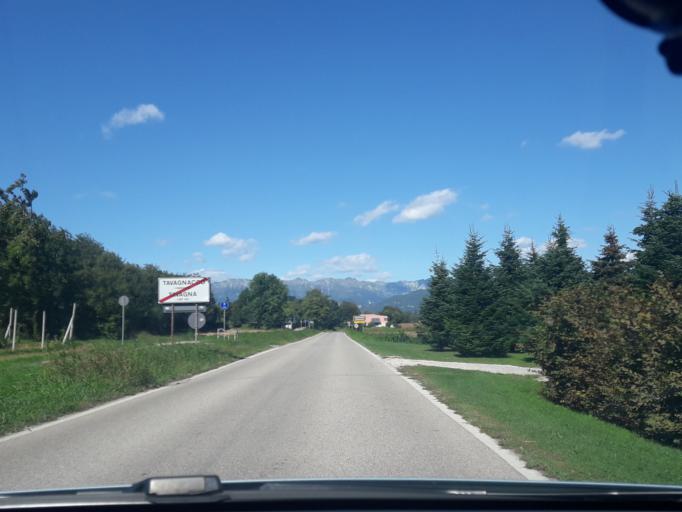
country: IT
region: Friuli Venezia Giulia
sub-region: Provincia di Udine
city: Reana del Roiale
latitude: 46.1349
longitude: 13.2164
